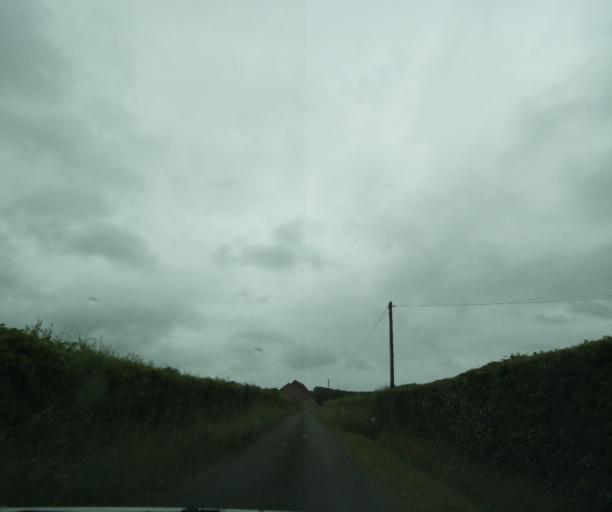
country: FR
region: Bourgogne
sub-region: Departement de Saone-et-Loire
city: Charolles
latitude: 46.4898
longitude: 4.2489
